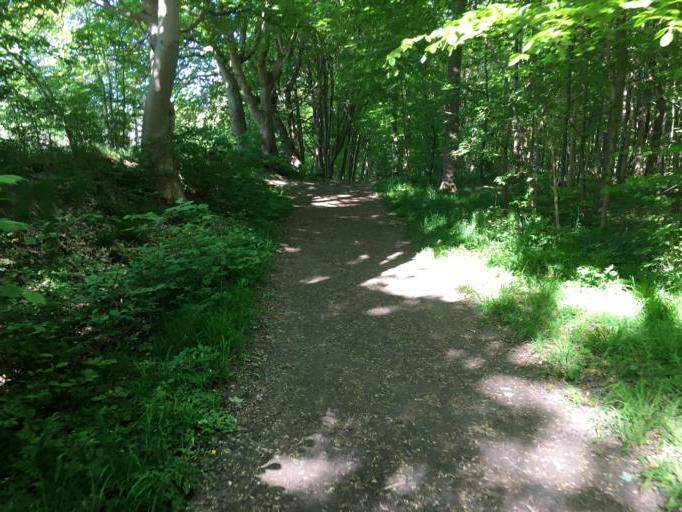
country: DK
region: Capital Region
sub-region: Ballerup Kommune
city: Ballerup
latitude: 55.7539
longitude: 12.3624
